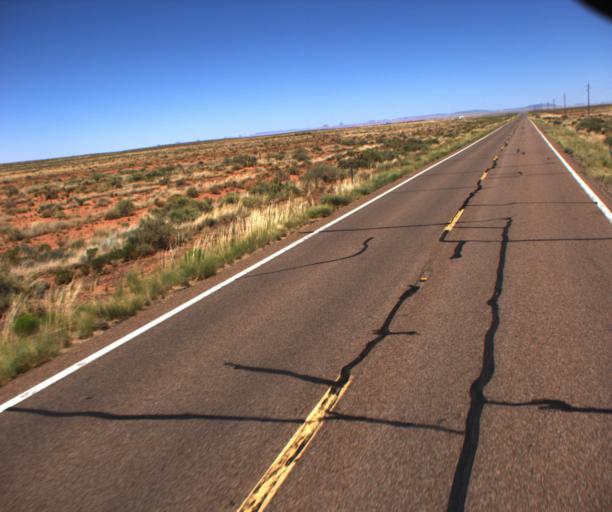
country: US
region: Arizona
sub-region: Coconino County
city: LeChee
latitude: 34.9514
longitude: -110.7605
